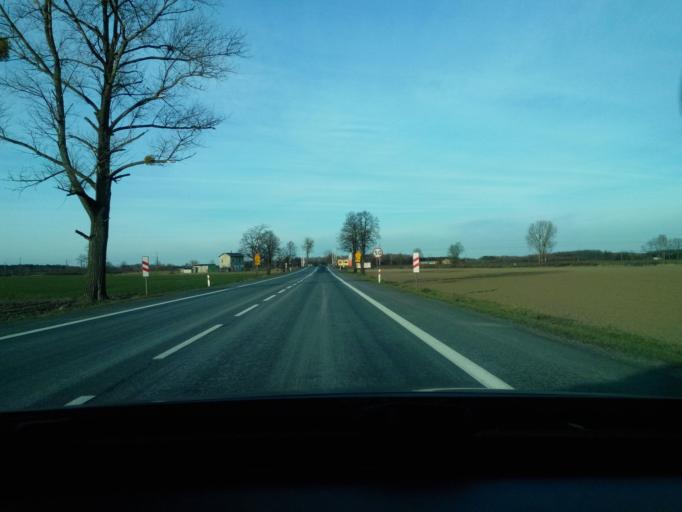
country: PL
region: Kujawsko-Pomorskie
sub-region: Powiat wloclawski
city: Lubien Kujawski
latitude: 52.3673
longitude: 19.1541
